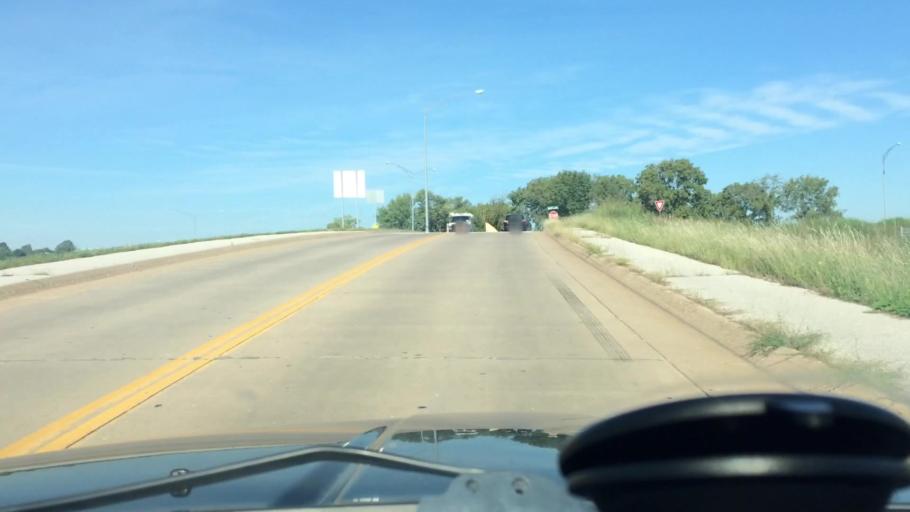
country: US
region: Missouri
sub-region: Greene County
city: Springfield
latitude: 37.1372
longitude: -93.2522
